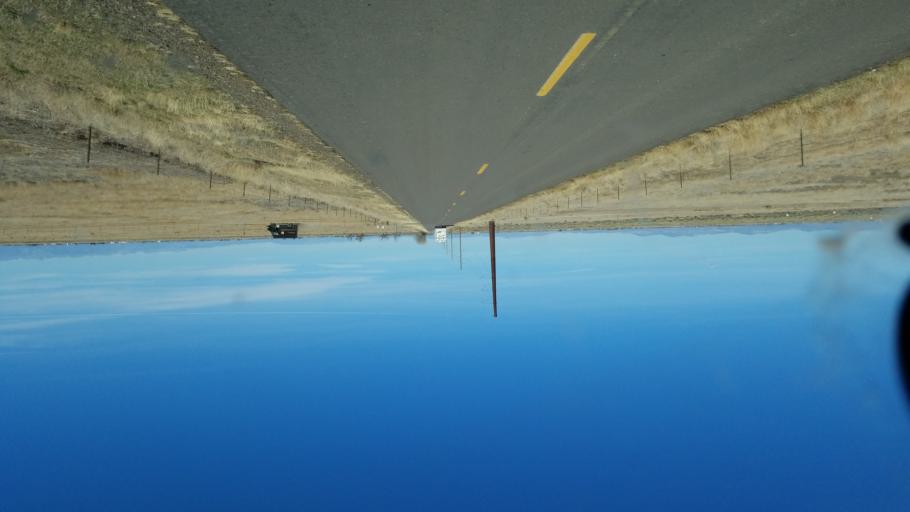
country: US
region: Colorado
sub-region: Rio Grande County
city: Monte Vista
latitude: 37.4723
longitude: -106.0942
